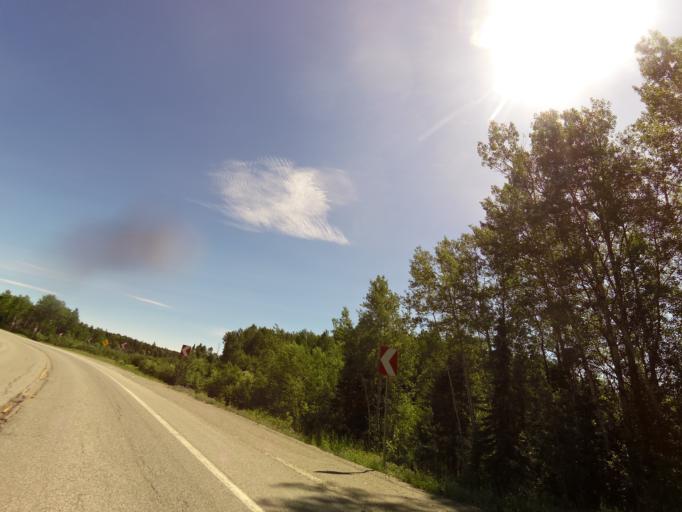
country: CA
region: Quebec
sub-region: Nord-du-Quebec
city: Lebel-sur-Quevillon
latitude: 48.8630
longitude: -77.1419
